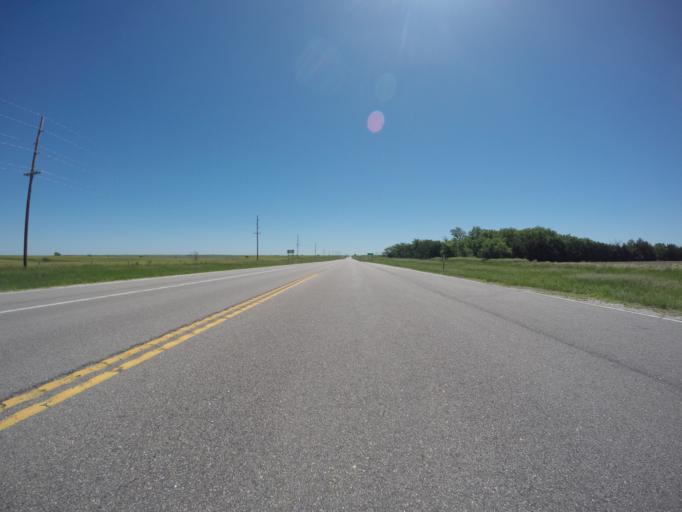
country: US
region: Kansas
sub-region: Norton County
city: Norton
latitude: 39.8284
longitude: -99.6830
